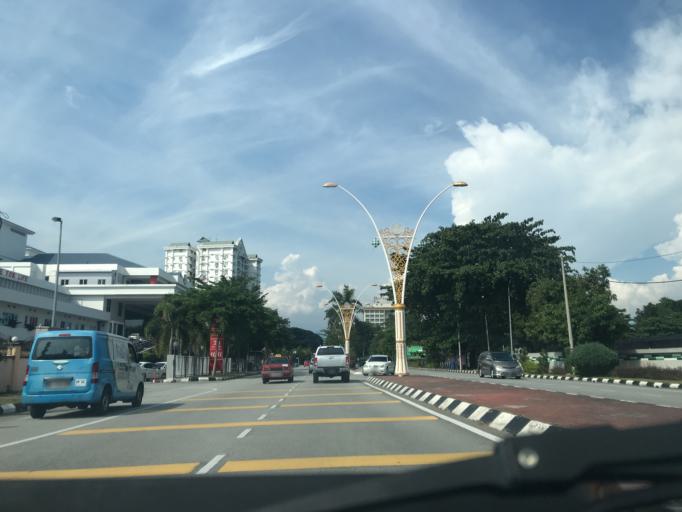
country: MY
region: Perak
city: Ipoh
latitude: 4.5938
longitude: 101.0953
